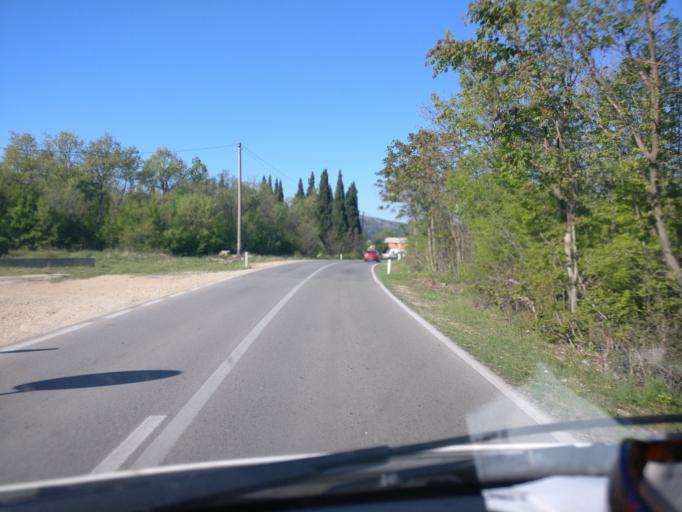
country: BA
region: Federation of Bosnia and Herzegovina
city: Tasovcici
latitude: 43.1272
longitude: 17.7623
